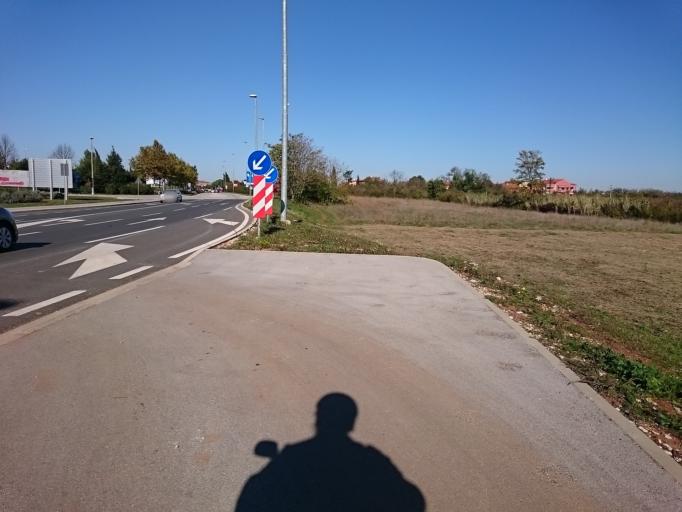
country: HR
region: Istarska
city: Umag
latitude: 45.4315
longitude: 13.5308
